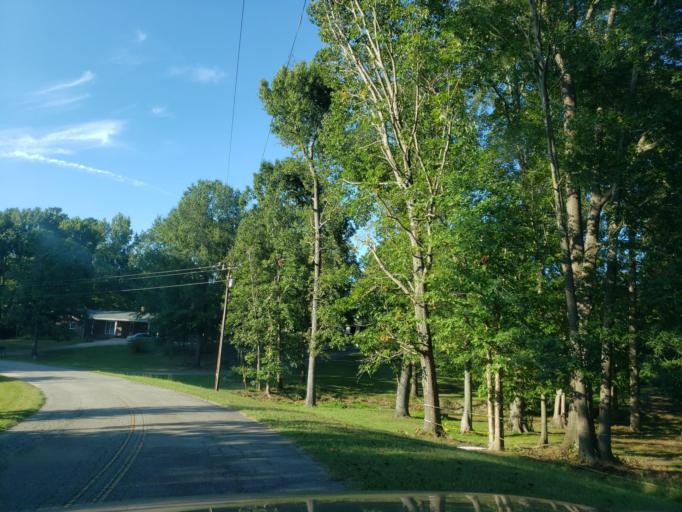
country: US
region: North Carolina
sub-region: Vance County
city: Henderson
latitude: 36.4061
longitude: -78.3753
